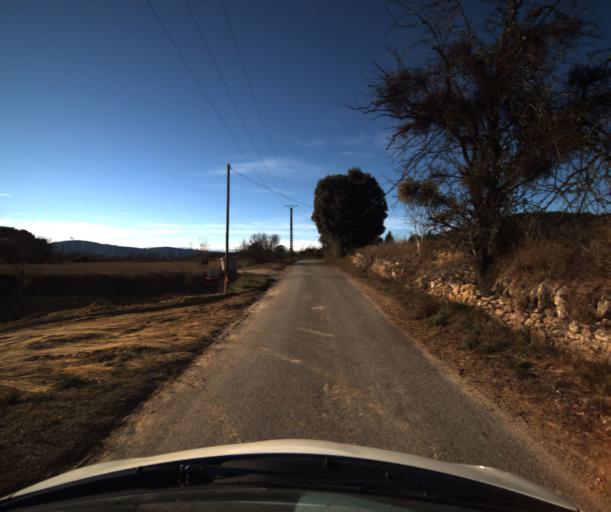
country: FR
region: Provence-Alpes-Cote d'Azur
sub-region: Departement du Vaucluse
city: Pertuis
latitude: 43.7026
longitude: 5.4792
